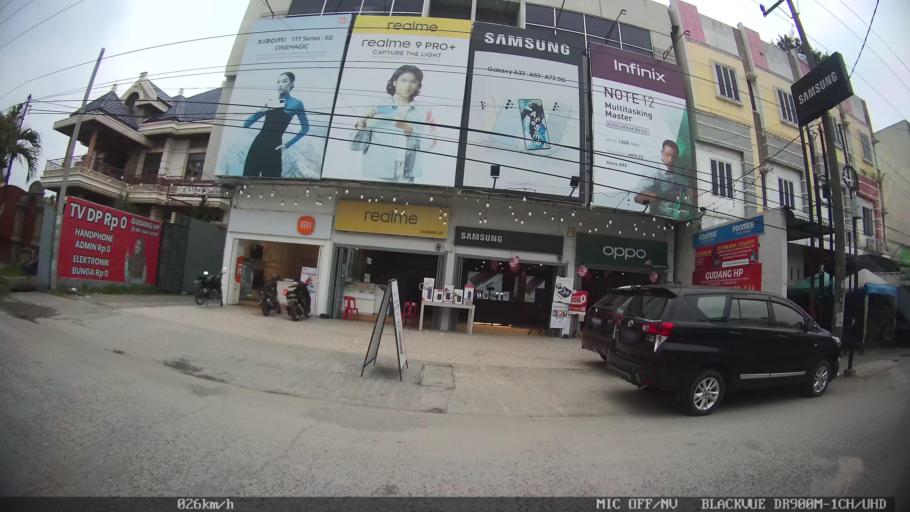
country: ID
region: North Sumatra
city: Medan
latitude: 3.5816
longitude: 98.7178
